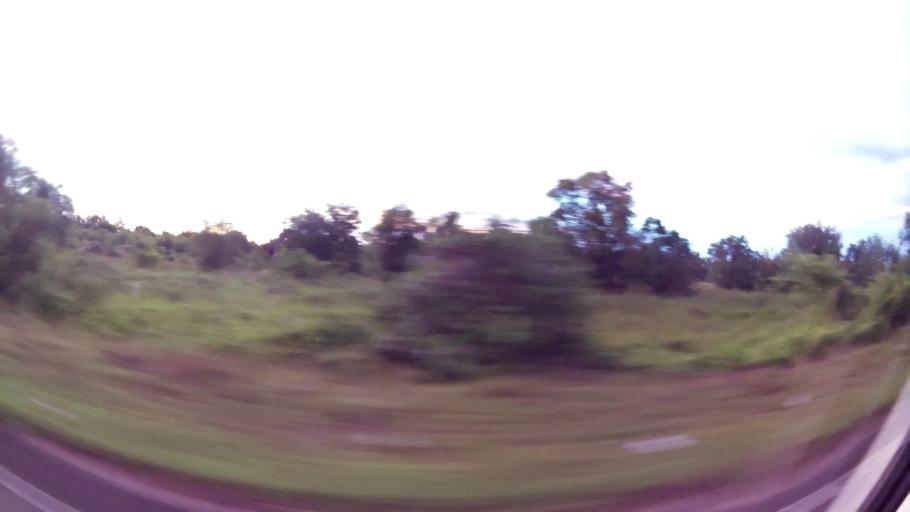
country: BN
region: Belait
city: Seria
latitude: 4.6351
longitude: 114.3915
